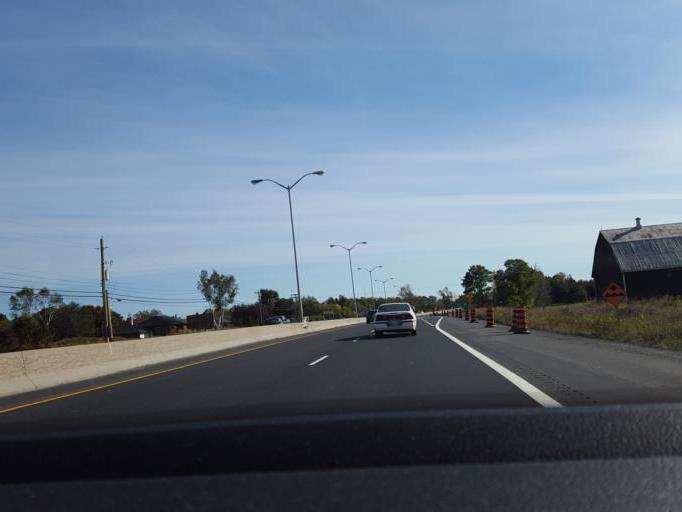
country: CA
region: Ontario
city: Oshawa
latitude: 43.9542
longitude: -78.6074
